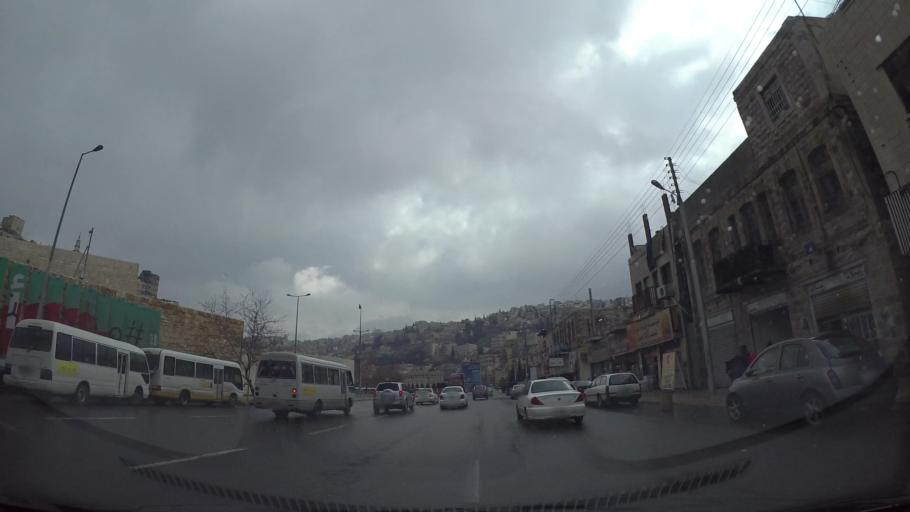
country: JO
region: Amman
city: Amman
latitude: 31.9449
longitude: 35.9274
